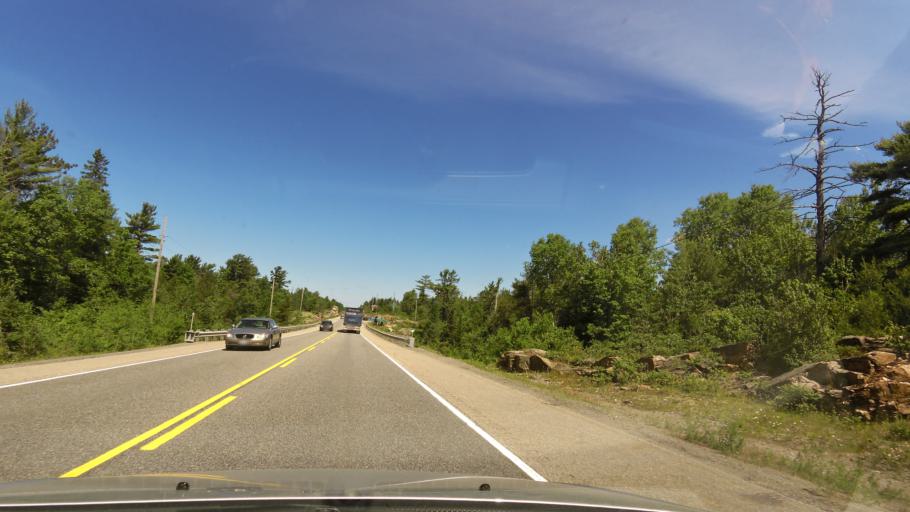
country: CA
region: Ontario
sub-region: Parry Sound District
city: Parry Sound
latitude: 45.6866
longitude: -80.4476
